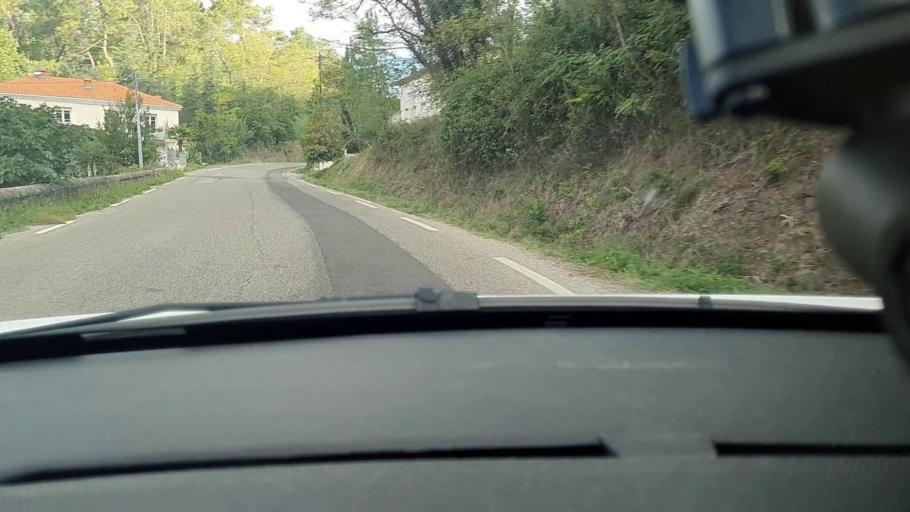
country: FR
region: Languedoc-Roussillon
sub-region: Departement du Gard
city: Besseges
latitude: 44.2984
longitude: 4.1270
